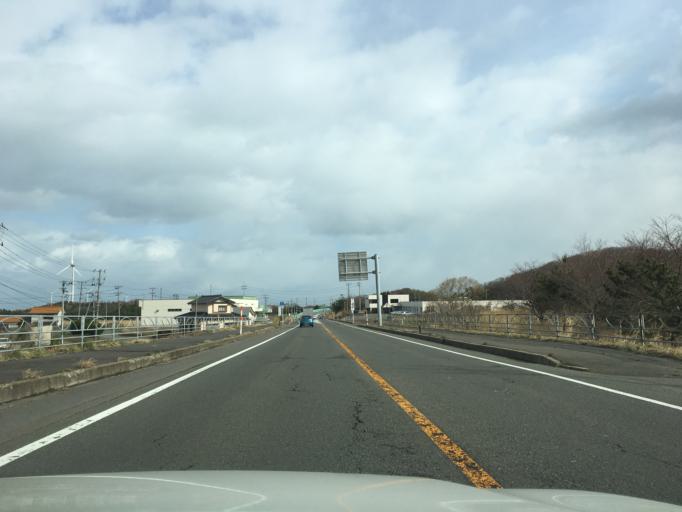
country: JP
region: Yamagata
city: Yuza
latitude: 39.2696
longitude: 139.9232
